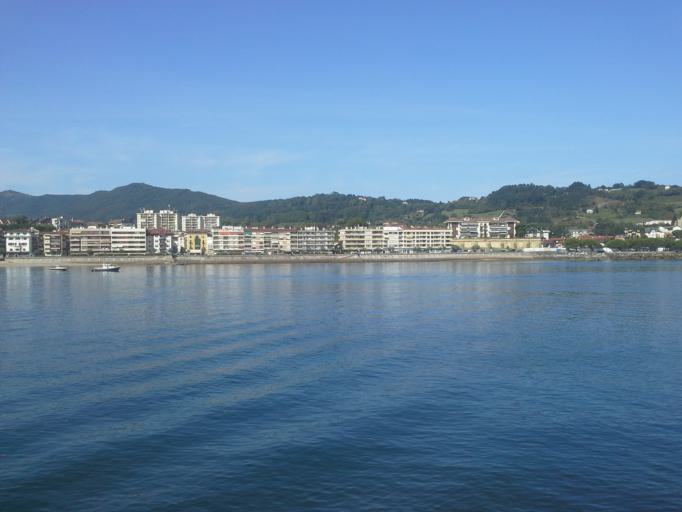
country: ES
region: Basque Country
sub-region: Provincia de Guipuzcoa
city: Fuenterrabia
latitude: 43.3703
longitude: -1.7878
